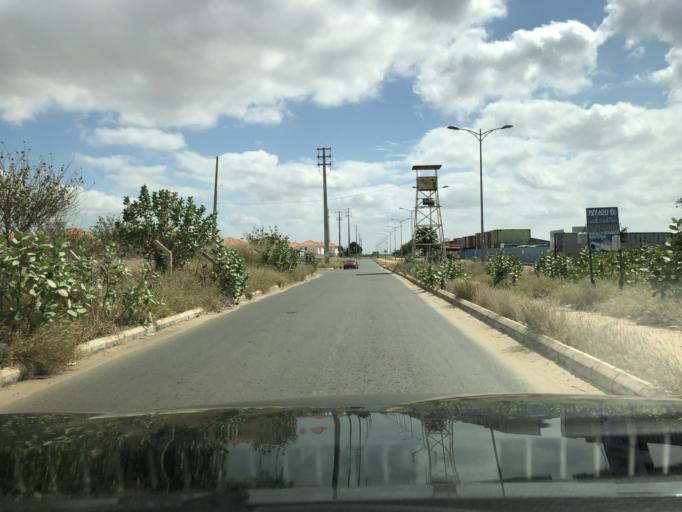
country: AO
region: Luanda
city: Luanda
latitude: -8.9725
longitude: 13.2414
